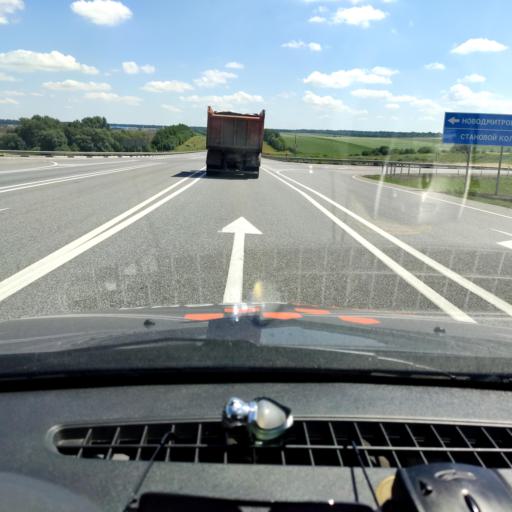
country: RU
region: Orjol
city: Zmiyevka
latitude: 52.8285
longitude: 36.2718
